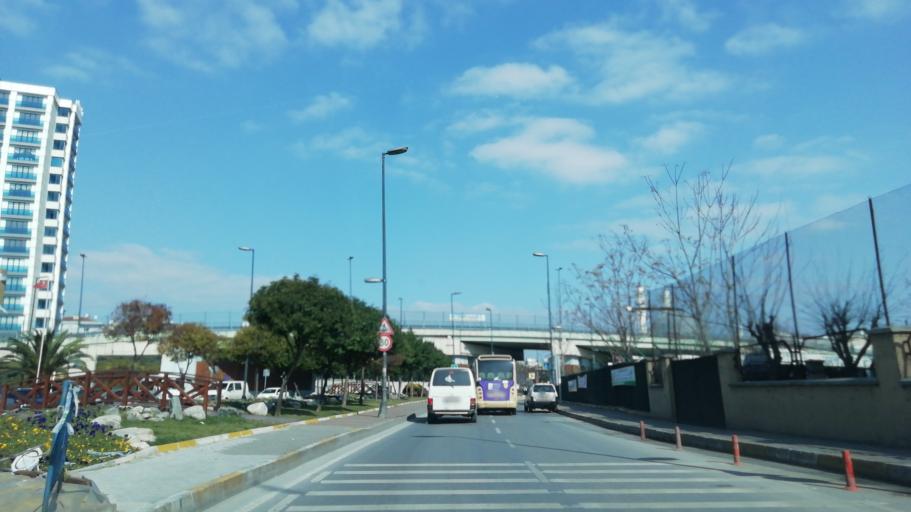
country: TR
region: Istanbul
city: Bahcelievler
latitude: 41.0126
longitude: 28.8474
